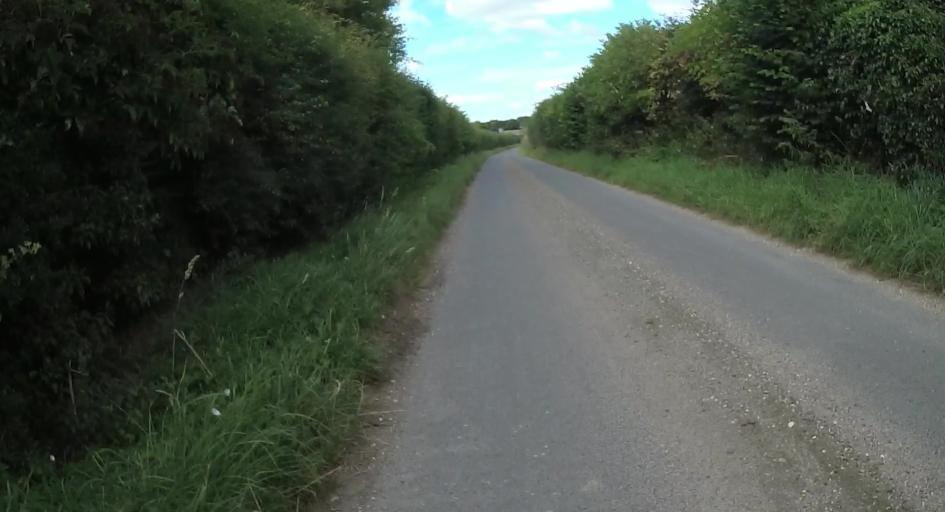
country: GB
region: England
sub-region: Hampshire
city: Kings Worthy
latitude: 51.1660
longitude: -1.2989
